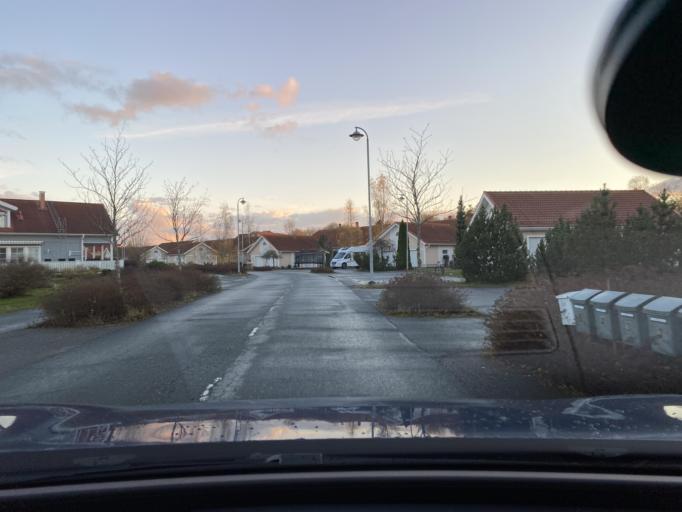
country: FI
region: Satakunta
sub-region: Pori
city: Huittinen
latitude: 61.1818
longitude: 22.7037
